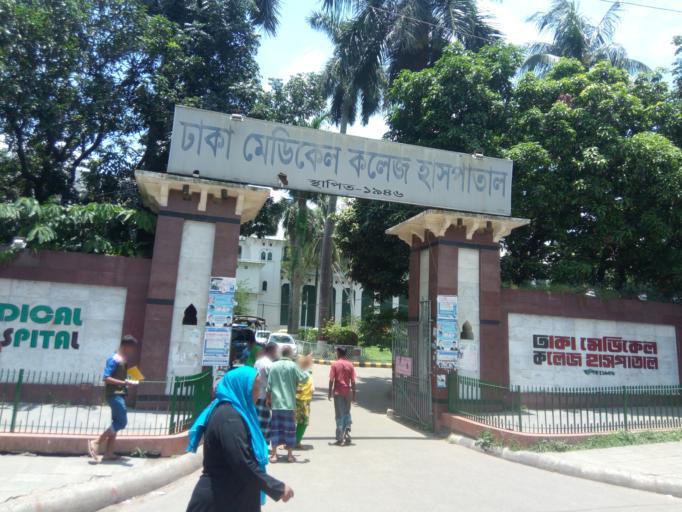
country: BD
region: Dhaka
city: Azimpur
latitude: 23.7262
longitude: 90.3986
